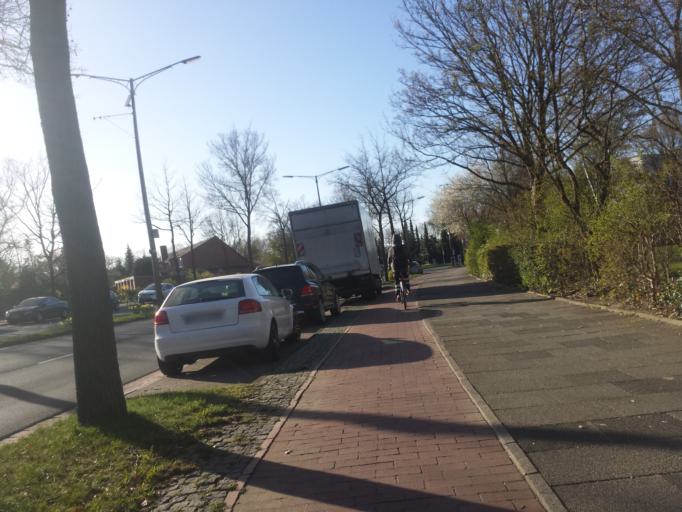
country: DE
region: Lower Saxony
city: Lilienthal
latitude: 53.0700
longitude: 8.9320
